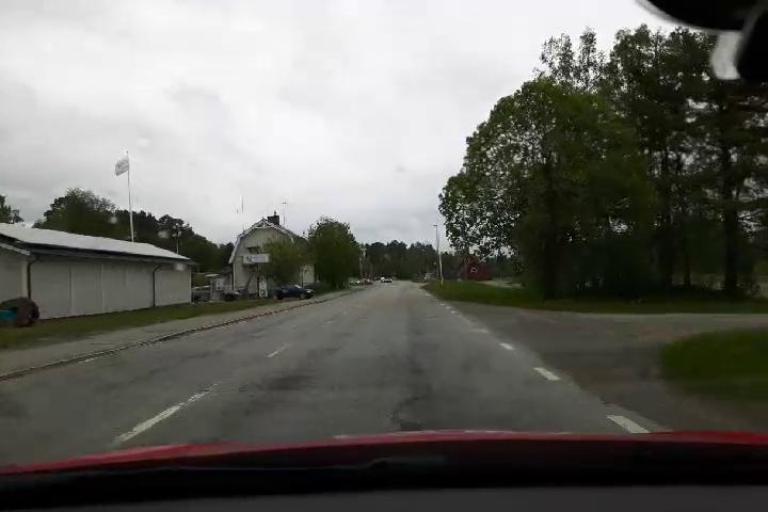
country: SE
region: Jaemtland
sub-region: Bergs Kommun
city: Hoverberg
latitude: 62.6451
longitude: 14.3721
